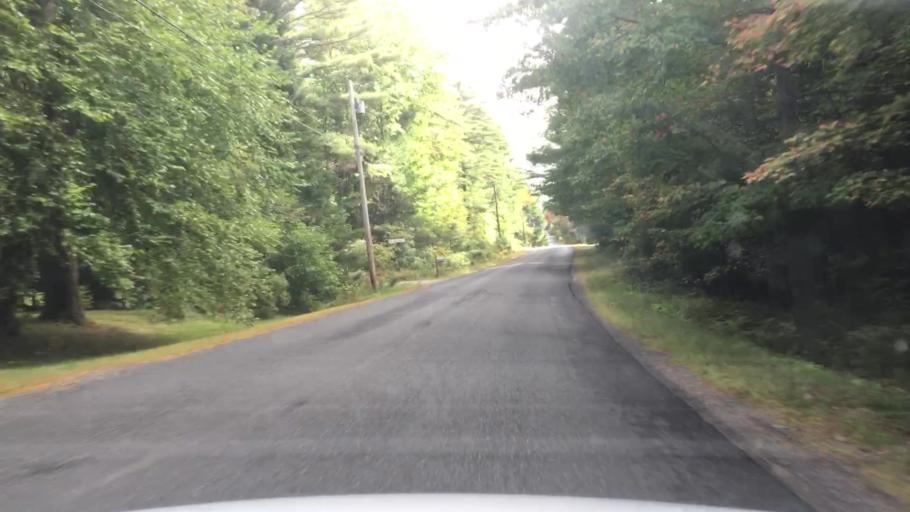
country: US
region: Maine
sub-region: Androscoggin County
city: Lisbon Falls
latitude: 43.9802
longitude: -70.0947
